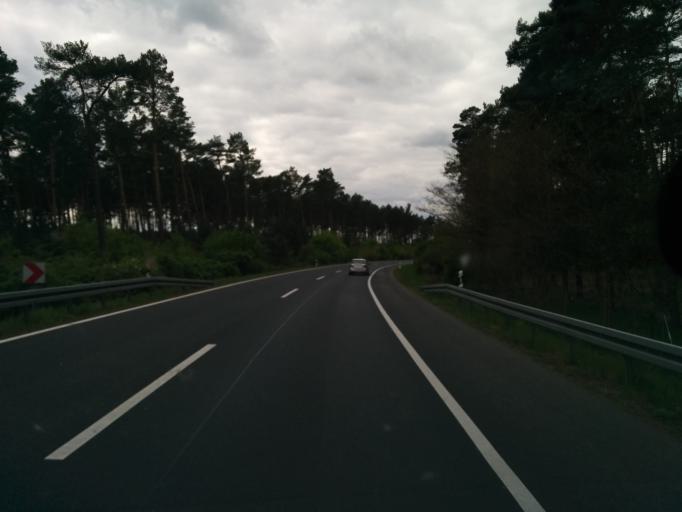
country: DE
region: Brandenburg
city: Gross Kreutz
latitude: 52.3406
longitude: 12.8140
